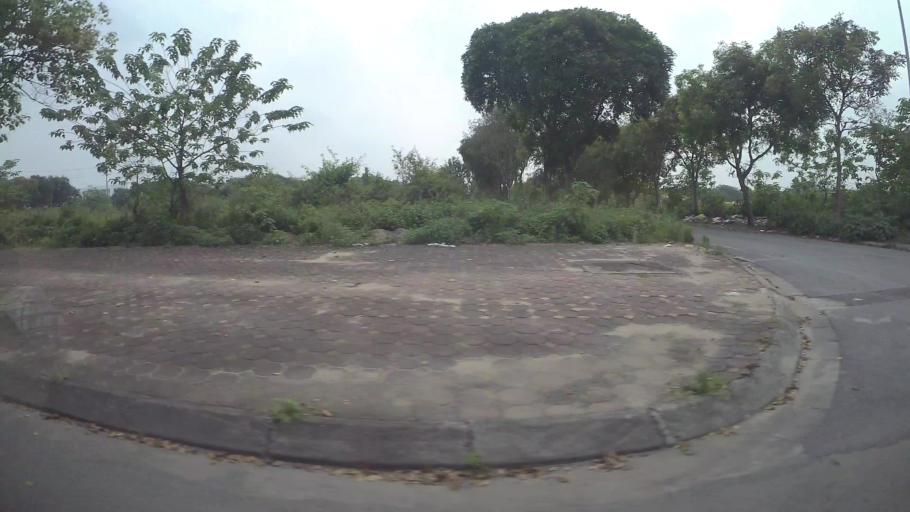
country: VN
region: Ha Noi
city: Trau Quy
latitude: 21.0664
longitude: 105.9024
